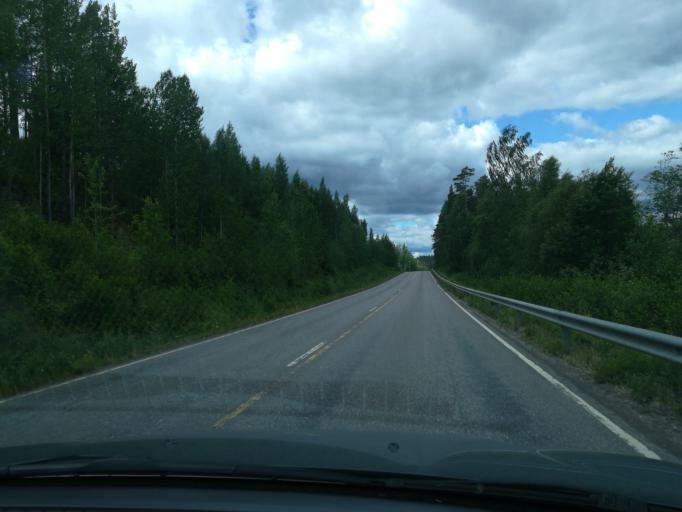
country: FI
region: Southern Savonia
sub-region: Mikkeli
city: Maentyharju
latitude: 61.3646
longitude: 26.9746
